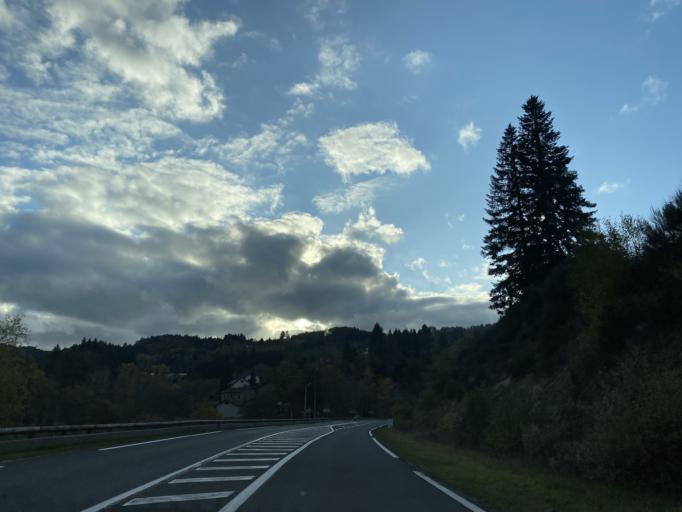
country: FR
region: Auvergne
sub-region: Departement du Puy-de-Dome
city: Job
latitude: 45.6459
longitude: 3.6704
